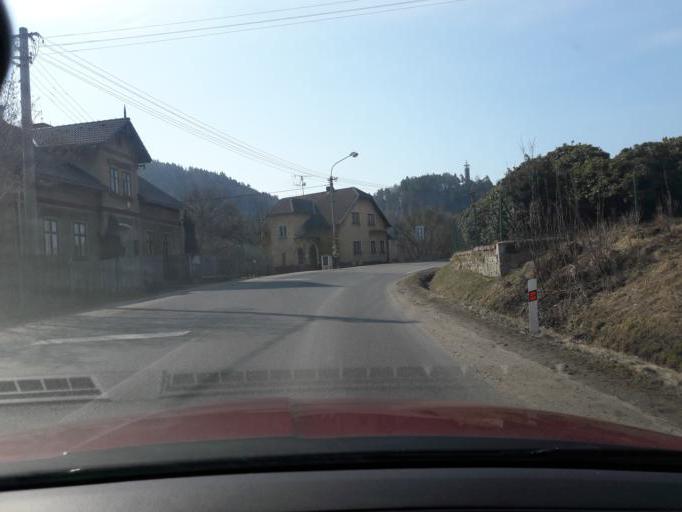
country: CZ
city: Novy Bor
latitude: 50.7381
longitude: 14.5875
